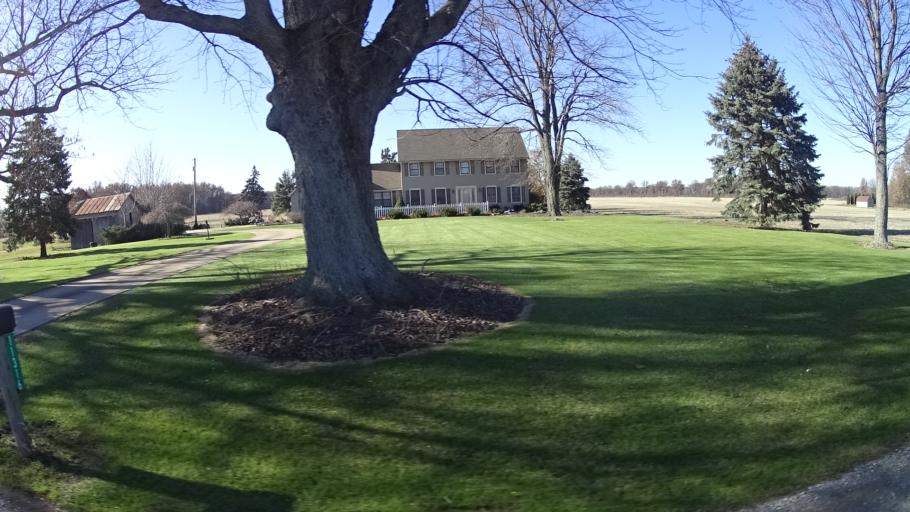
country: US
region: Ohio
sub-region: Lorain County
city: Elyria
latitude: 41.3240
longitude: -82.1518
